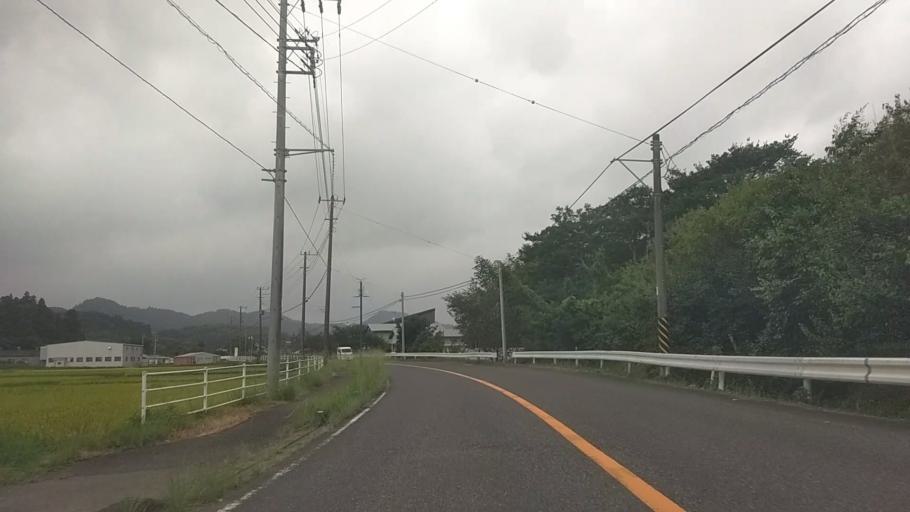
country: JP
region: Chiba
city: Kawaguchi
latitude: 35.1372
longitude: 139.9959
